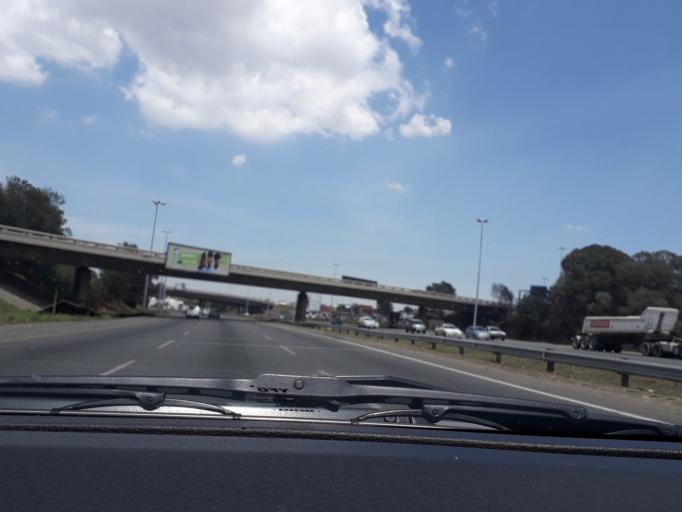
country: ZA
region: Gauteng
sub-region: City of Johannesburg Metropolitan Municipality
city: Johannesburg
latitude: -26.2557
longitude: 27.9905
